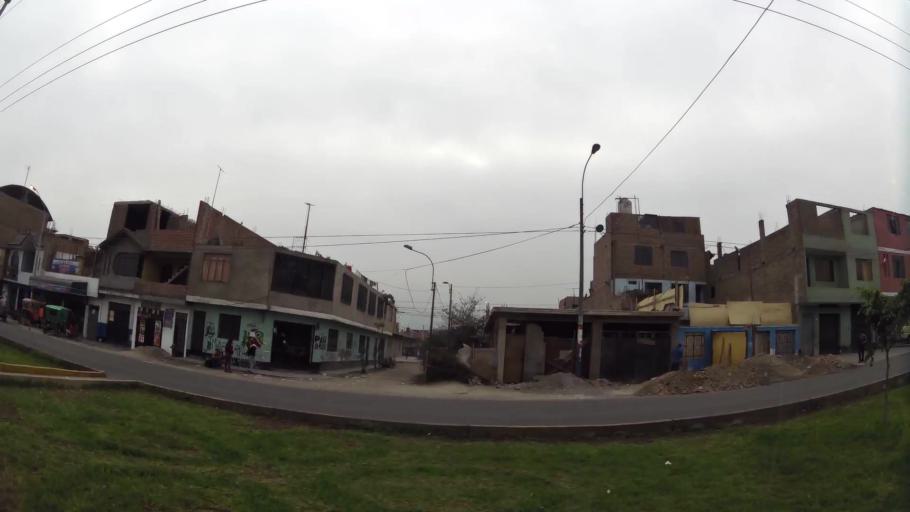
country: PE
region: Lima
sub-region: Lima
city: Independencia
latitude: -11.9618
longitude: -76.9849
